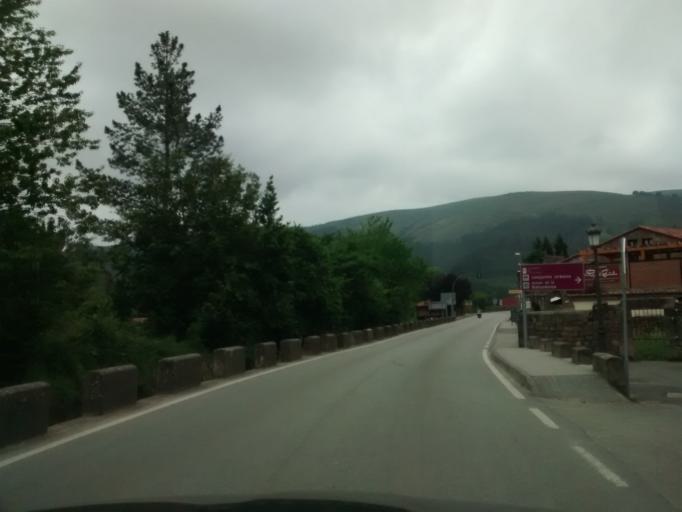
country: ES
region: Cantabria
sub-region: Provincia de Cantabria
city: Cabezon de la Sal
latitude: 43.2942
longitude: -4.2370
